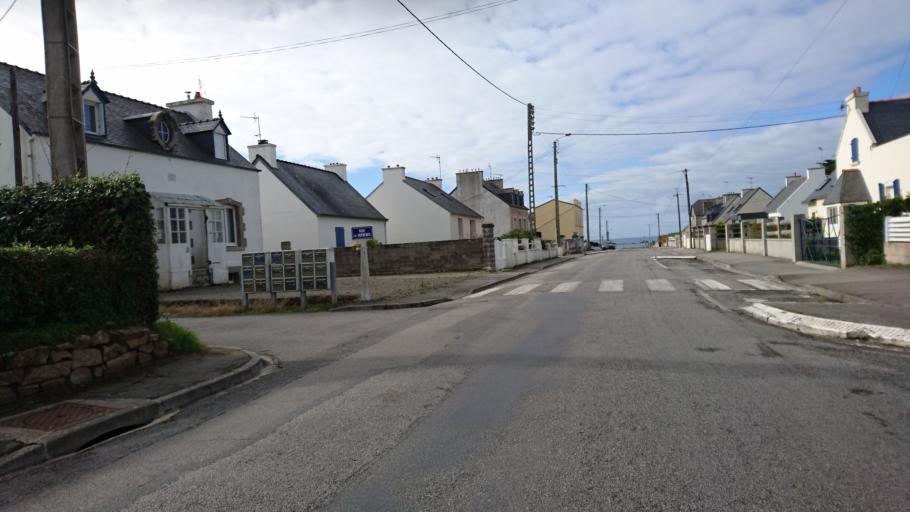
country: FR
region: Brittany
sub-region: Departement du Finistere
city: Lampaul-Plouarzel
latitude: 48.4478
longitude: -4.7695
